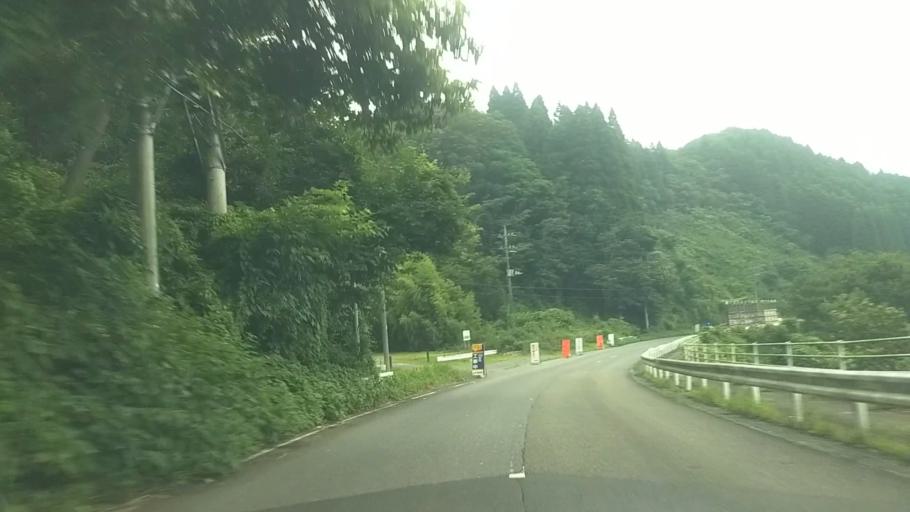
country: JP
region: Chiba
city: Katsuura
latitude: 35.2556
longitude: 140.2437
